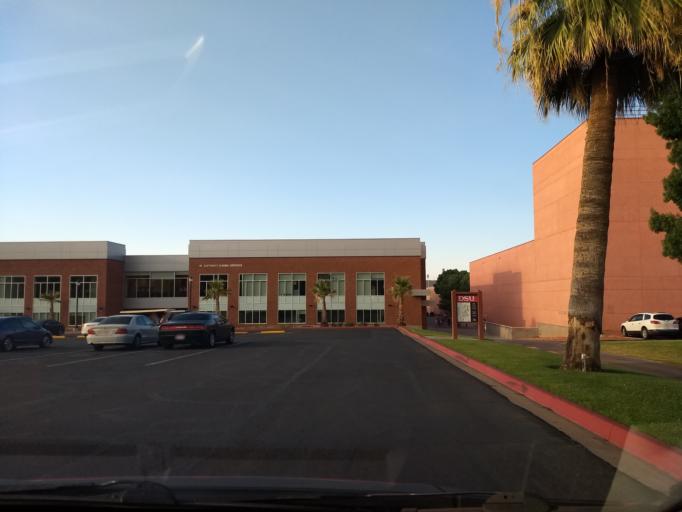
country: US
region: Utah
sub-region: Washington County
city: Saint George
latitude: 37.1025
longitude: -113.5674
